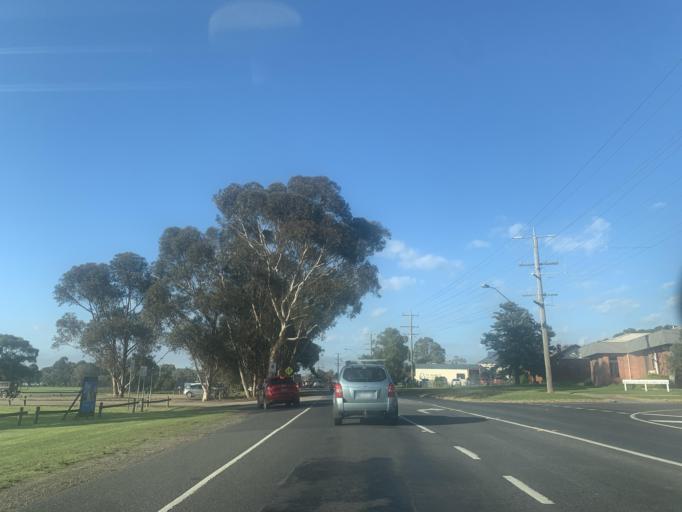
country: AU
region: Victoria
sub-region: Mornington Peninsula
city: Hastings
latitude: -38.3027
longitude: 145.1917
